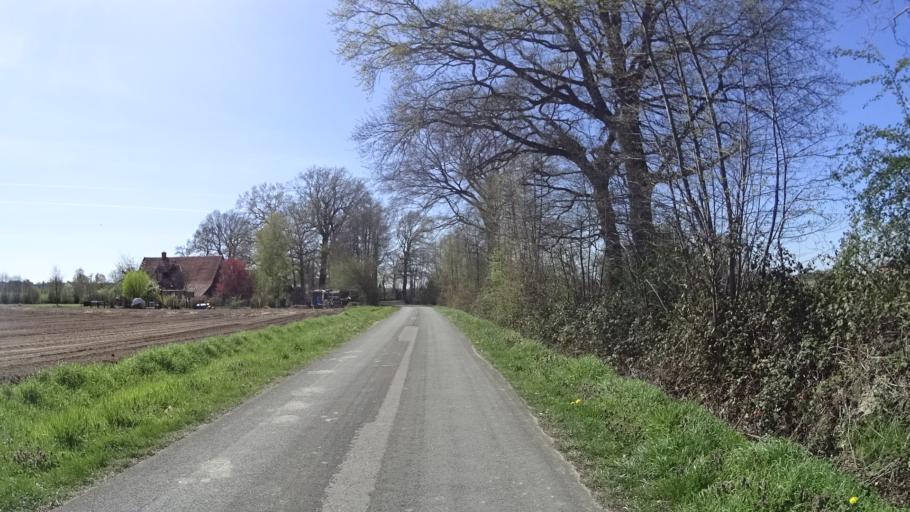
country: DE
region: North Rhine-Westphalia
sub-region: Regierungsbezirk Munster
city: Dulmen
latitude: 51.8067
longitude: 7.3393
